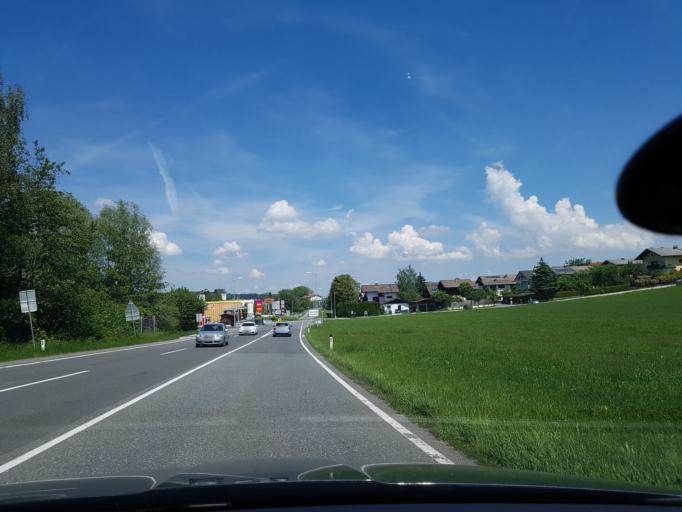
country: AT
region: Salzburg
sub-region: Politischer Bezirk Salzburg-Umgebung
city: Obertrum am See
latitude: 47.9311
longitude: 13.0811
